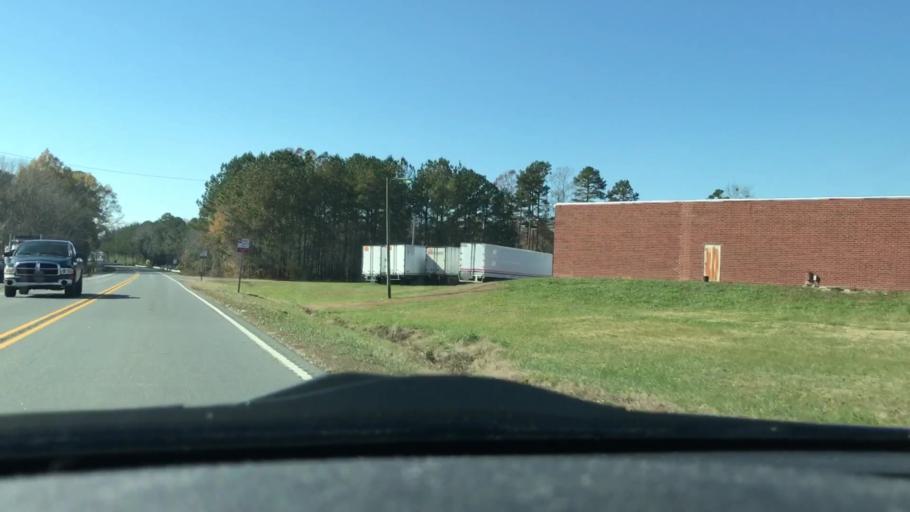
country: US
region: North Carolina
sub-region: Stanly County
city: Albemarle
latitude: 35.4771
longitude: -80.2540
